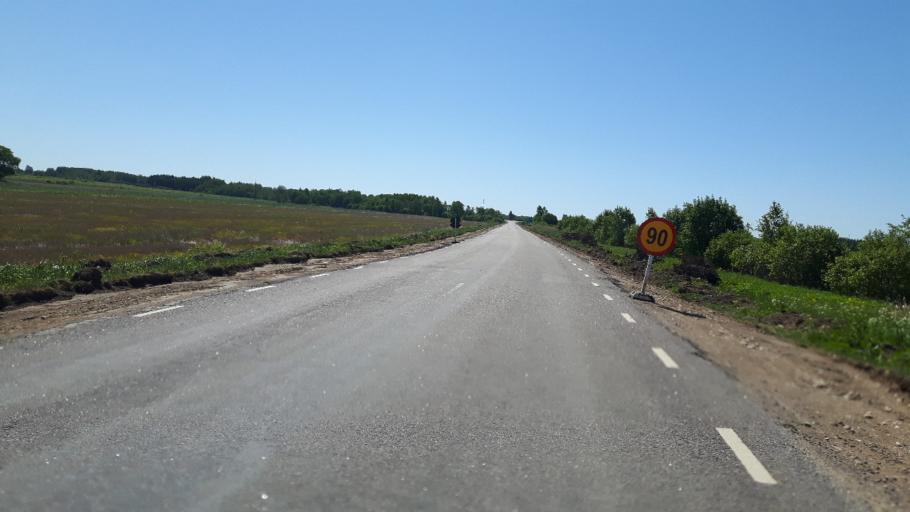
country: EE
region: Ida-Virumaa
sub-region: Narva-Joesuu linn
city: Narva-Joesuu
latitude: 59.3858
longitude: 27.9205
